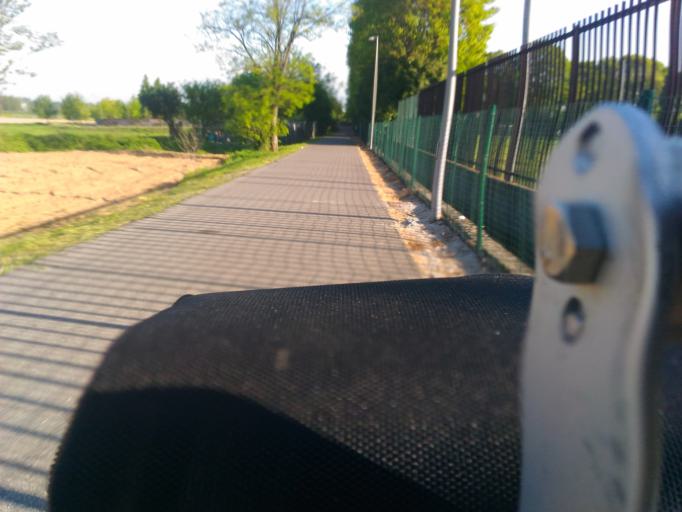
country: IT
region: Lombardy
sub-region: Citta metropolitana di Milano
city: Vizzolo Predabissi
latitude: 45.3575
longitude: 9.3451
